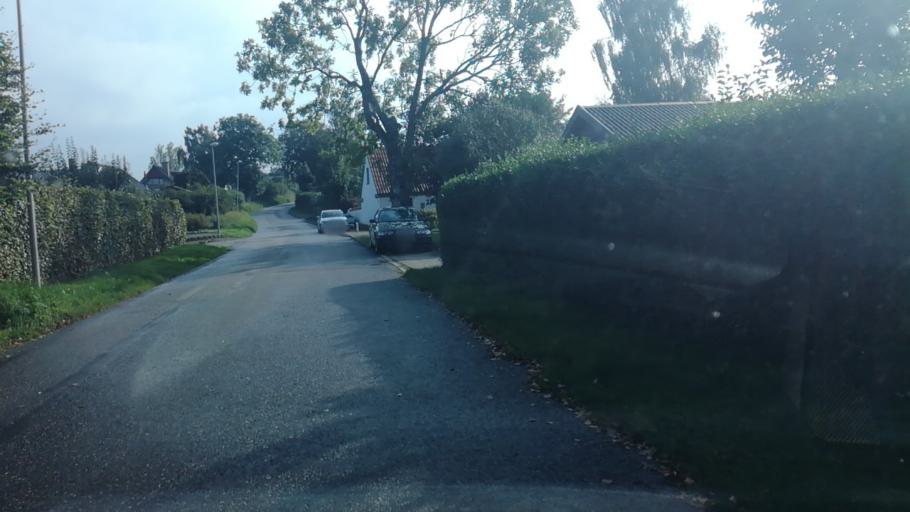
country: DK
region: South Denmark
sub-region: Fredericia Kommune
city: Fredericia
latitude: 55.6211
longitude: 9.7884
